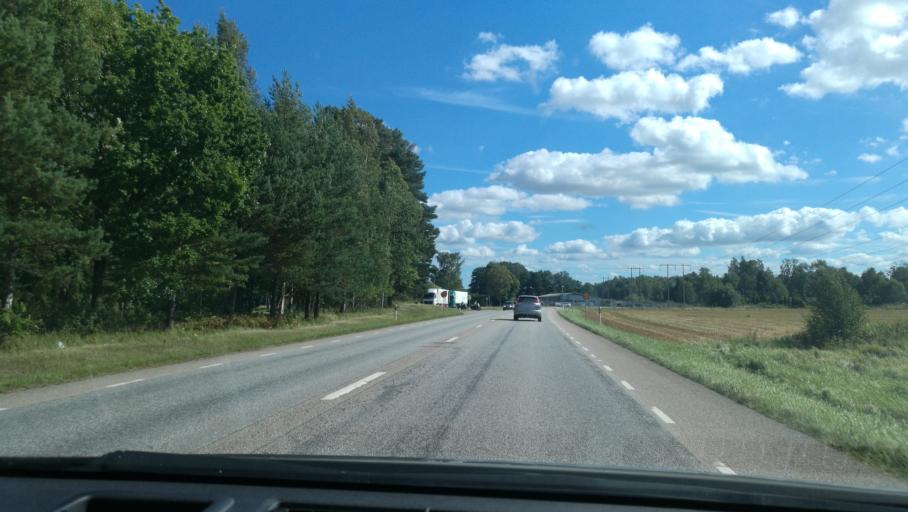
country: SE
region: Vaestra Goetaland
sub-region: Lidkopings Kommun
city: Vinninga
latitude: 58.4919
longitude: 13.2313
